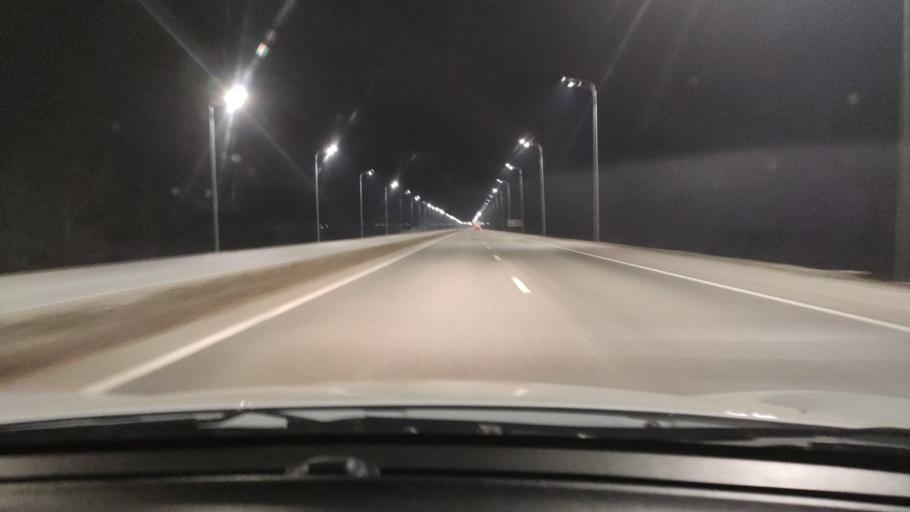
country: RU
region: Tatarstan
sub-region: Alekseyevskiy Rayon
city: Alekseyevskoye
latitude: 55.3239
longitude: 50.0331
